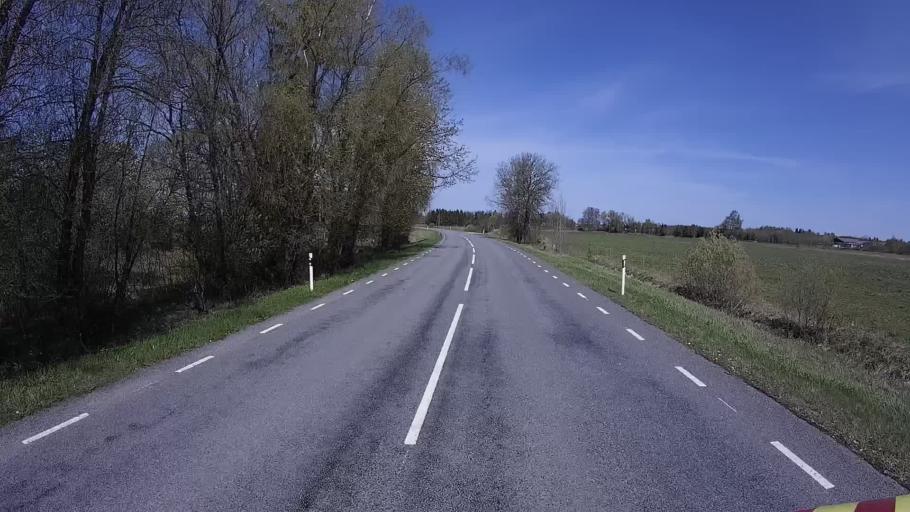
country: EE
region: Laeaene
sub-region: Lihula vald
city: Lihula
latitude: 58.6651
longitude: 23.8344
